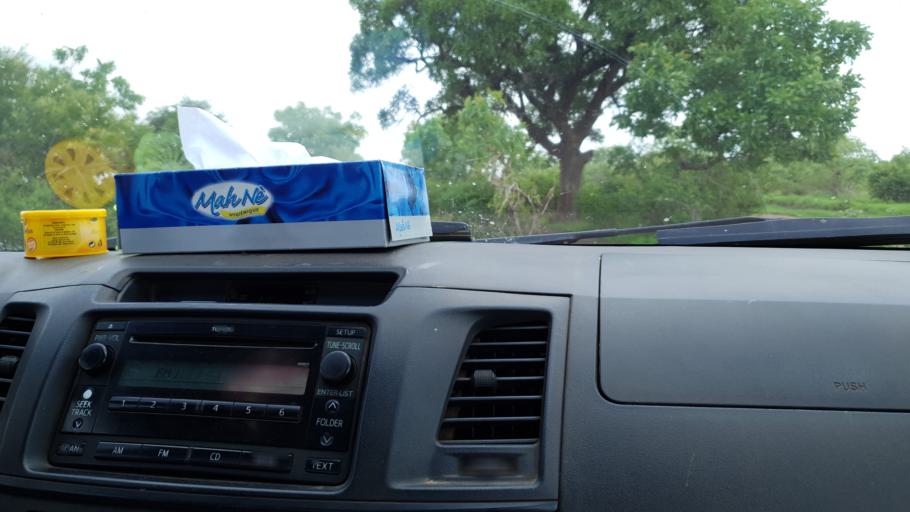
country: ML
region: Segou
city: Baroueli
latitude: 13.3471
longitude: -7.0940
